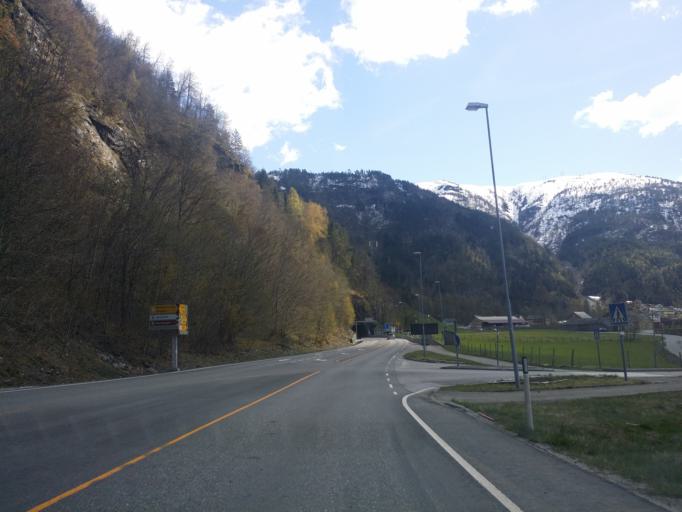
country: NO
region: Hordaland
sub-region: Granvin
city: Granvin
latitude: 60.5350
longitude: 6.7339
